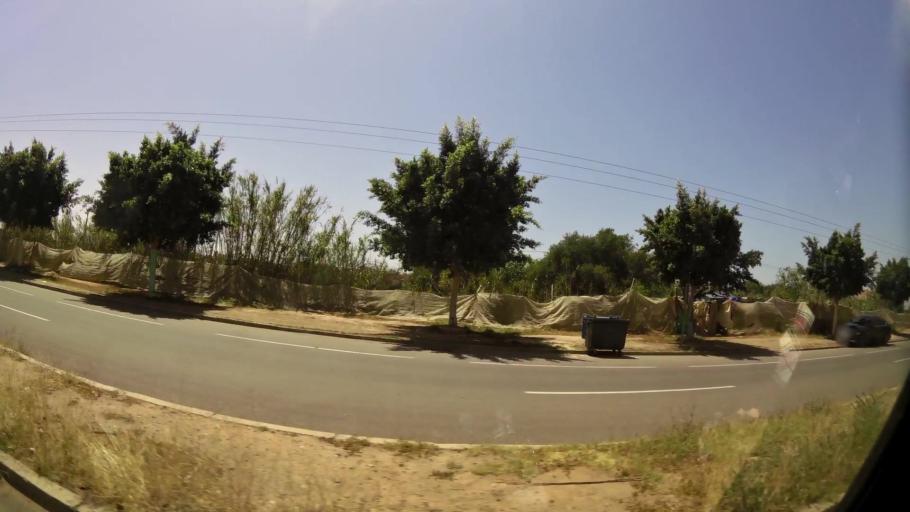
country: MA
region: Souss-Massa-Draa
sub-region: Inezgane-Ait Mellou
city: Inezgane
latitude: 30.3506
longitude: -9.4866
